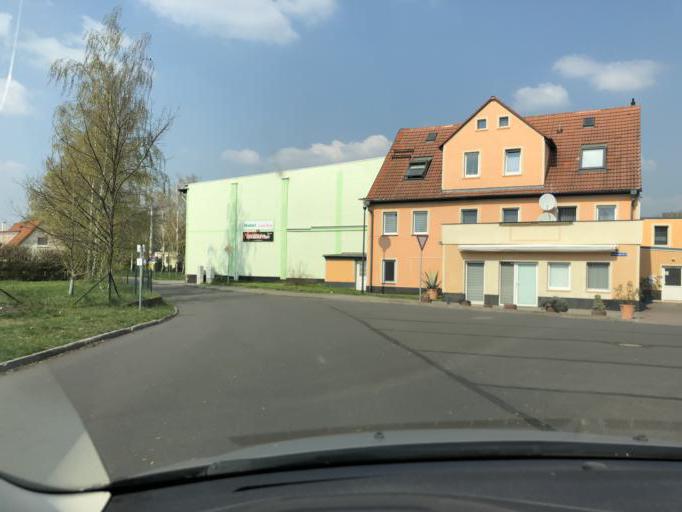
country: DE
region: Saxony-Anhalt
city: Landsberg
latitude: 51.5321
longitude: 12.1487
